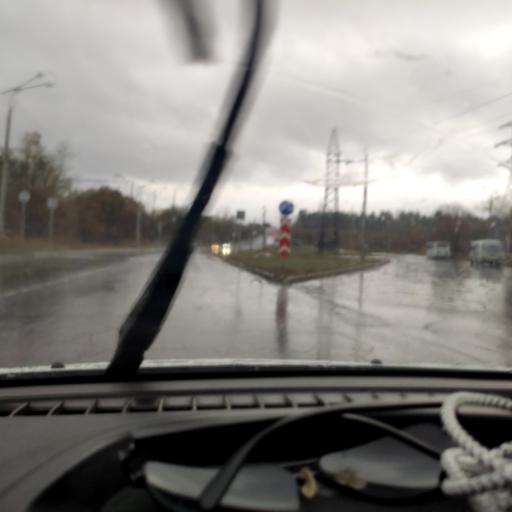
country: RU
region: Samara
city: Zhigulevsk
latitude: 53.4734
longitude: 49.5380
